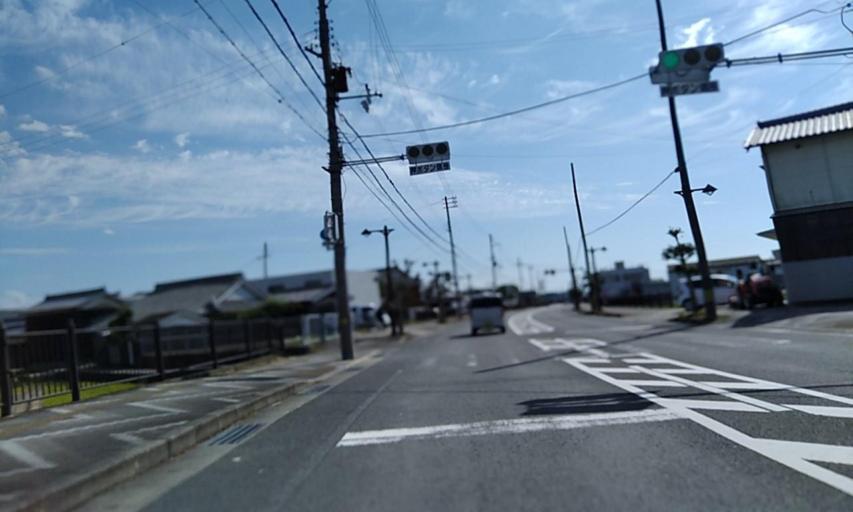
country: JP
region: Wakayama
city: Gobo
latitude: 33.9050
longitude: 135.1609
